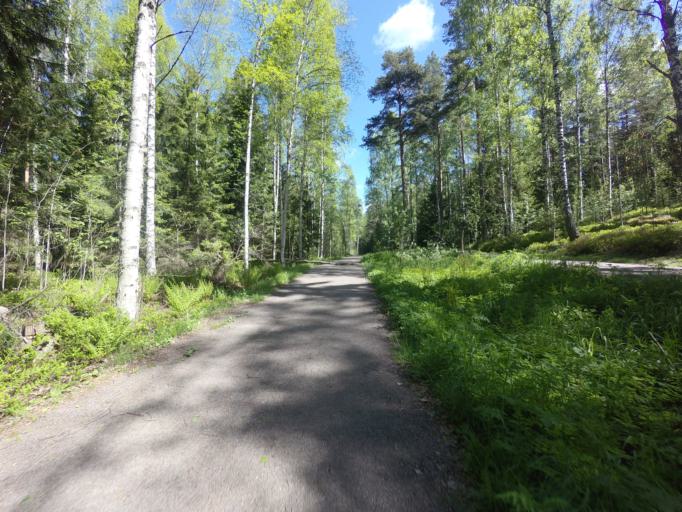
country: FI
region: Uusimaa
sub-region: Helsinki
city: Kauniainen
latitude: 60.1816
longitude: 24.7238
